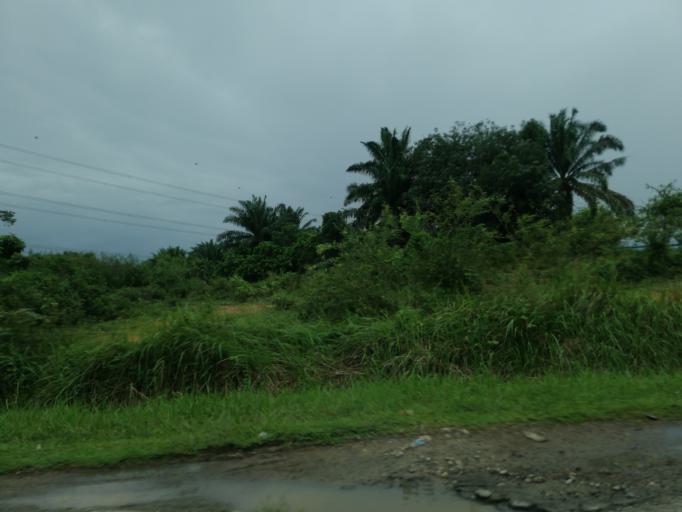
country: MY
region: Penang
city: Tasek Glugor
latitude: 5.4909
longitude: 100.6043
